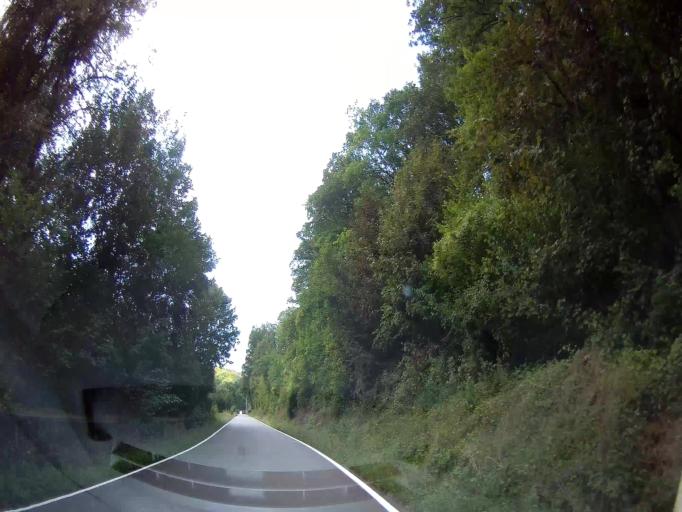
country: BE
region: Wallonia
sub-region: Province de Namur
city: Onhaye
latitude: 50.2925
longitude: 4.8082
